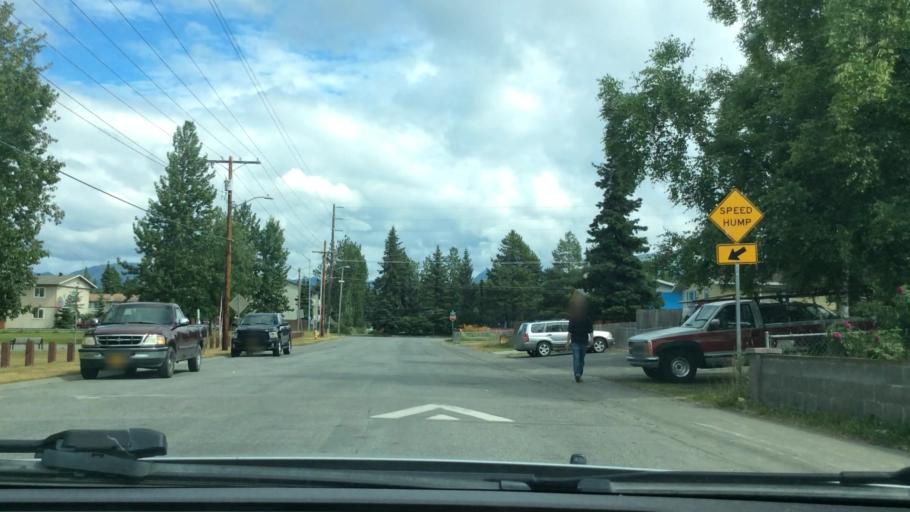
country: US
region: Alaska
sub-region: Anchorage Municipality
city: Anchorage
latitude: 61.2206
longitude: -149.7959
